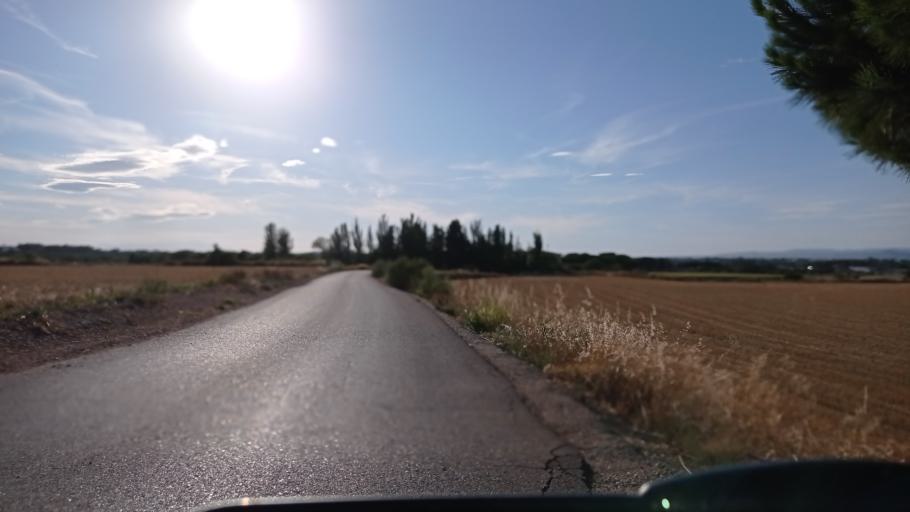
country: ES
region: Aragon
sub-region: Provincia de Zaragoza
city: Oliver-Valdefierro, Oliver, Valdefierro
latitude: 41.6694
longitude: -0.9650
